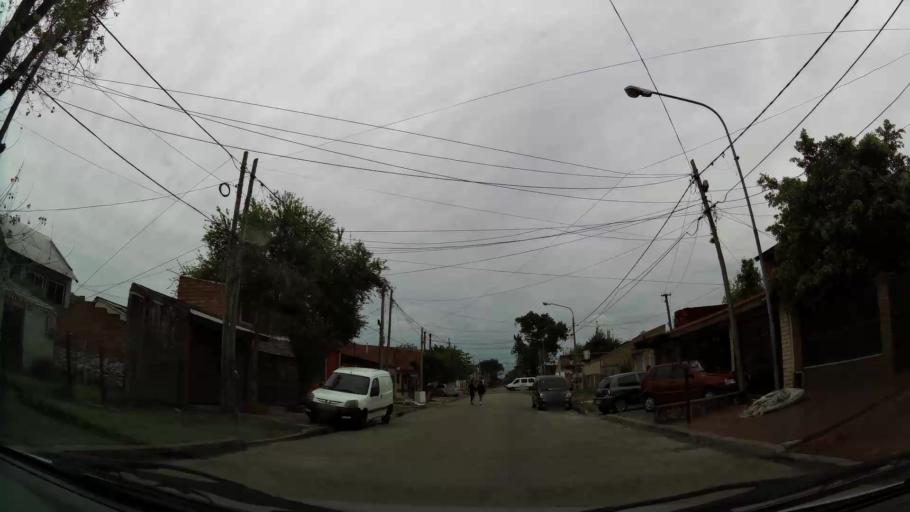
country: AR
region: Buenos Aires
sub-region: Partido de Lanus
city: Lanus
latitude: -34.7239
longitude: -58.3710
